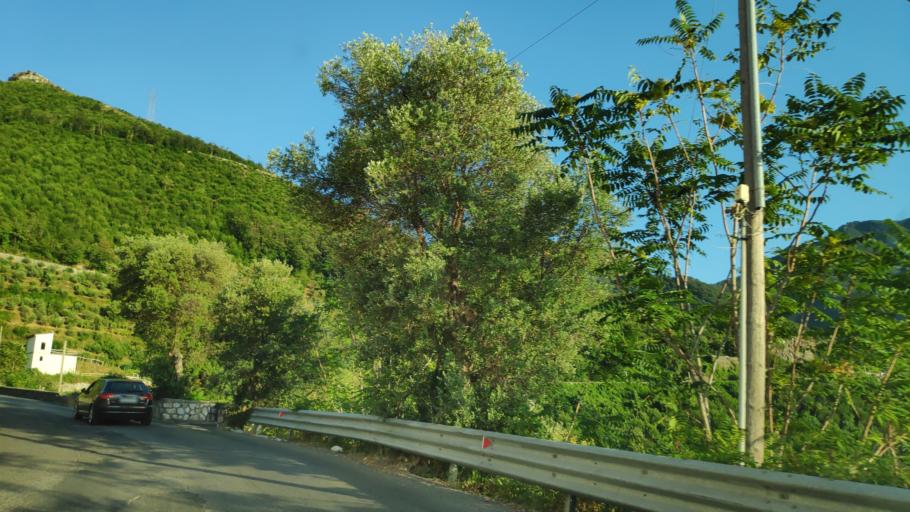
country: IT
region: Campania
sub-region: Provincia di Salerno
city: Corbara
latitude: 40.7224
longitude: 14.5993
